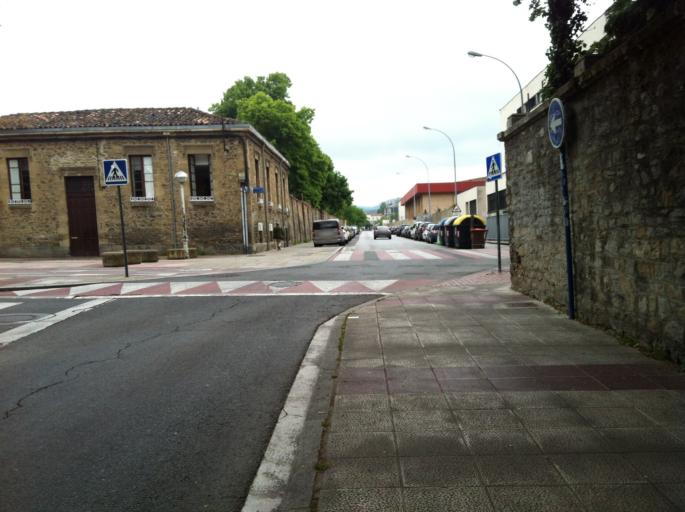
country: ES
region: Basque Country
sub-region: Provincia de Alava
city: Gasteiz / Vitoria
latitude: 42.8416
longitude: -2.6773
